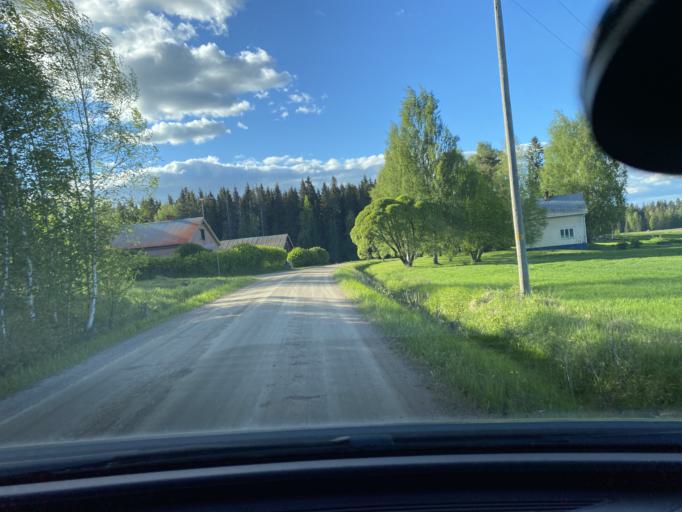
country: FI
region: Satakunta
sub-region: Pori
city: Huittinen
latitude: 61.1357
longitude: 22.8340
